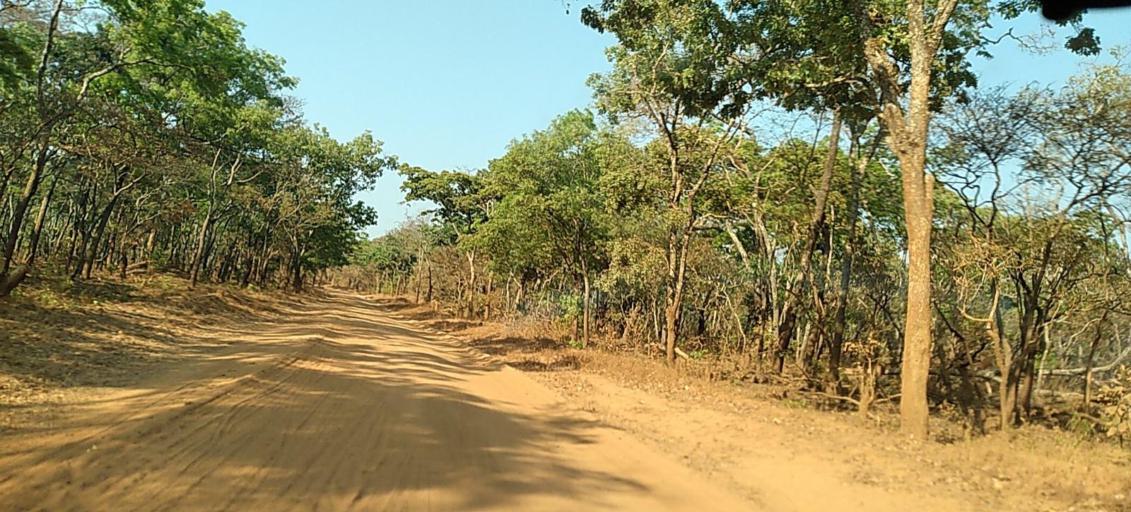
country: ZM
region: North-Western
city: Kasempa
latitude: -13.5617
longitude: 25.9986
